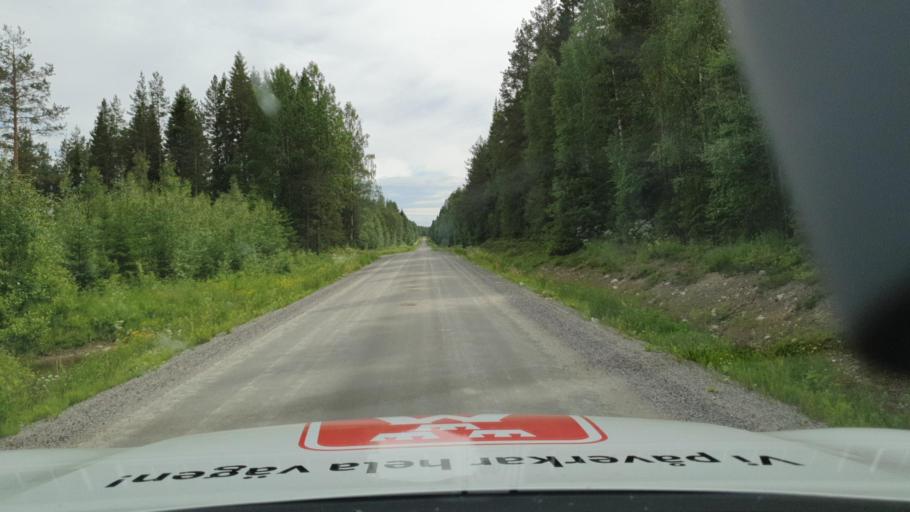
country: SE
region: Vaesterbotten
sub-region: Skelleftea Kommun
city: Burea
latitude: 64.4373
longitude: 21.0163
